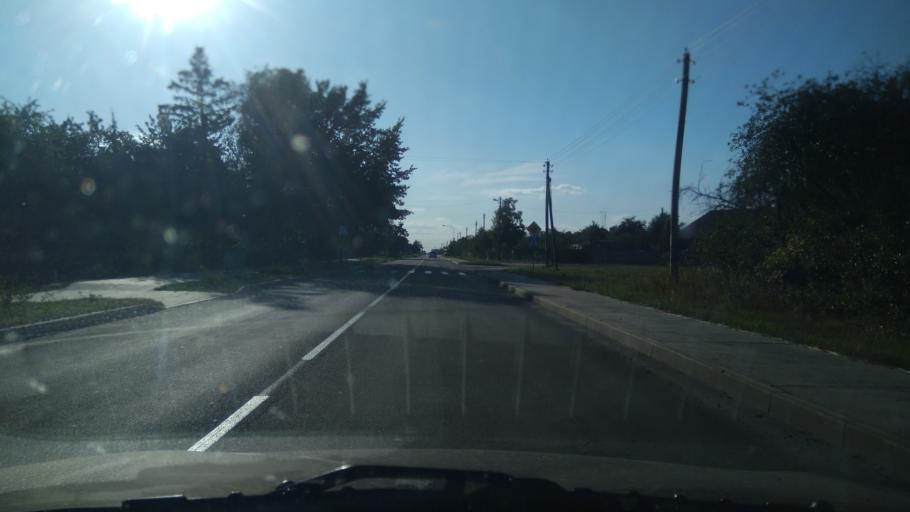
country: BY
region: Brest
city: Byaroza
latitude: 52.5426
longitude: 24.9704
